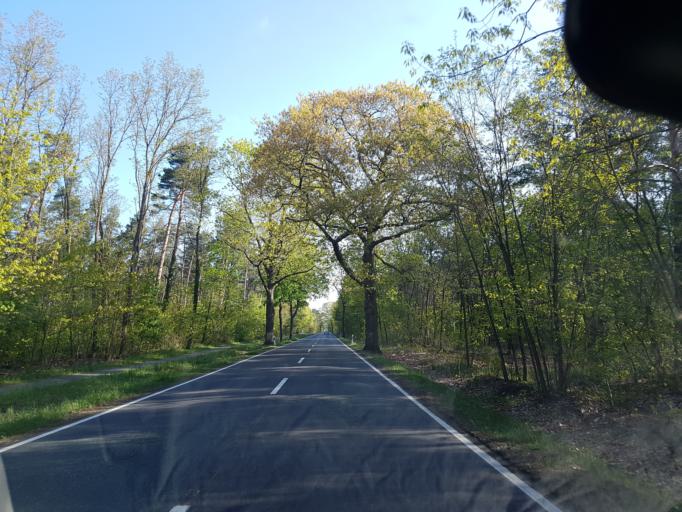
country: DE
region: Brandenburg
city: Grossraschen
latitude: 51.6023
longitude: 14.0170
